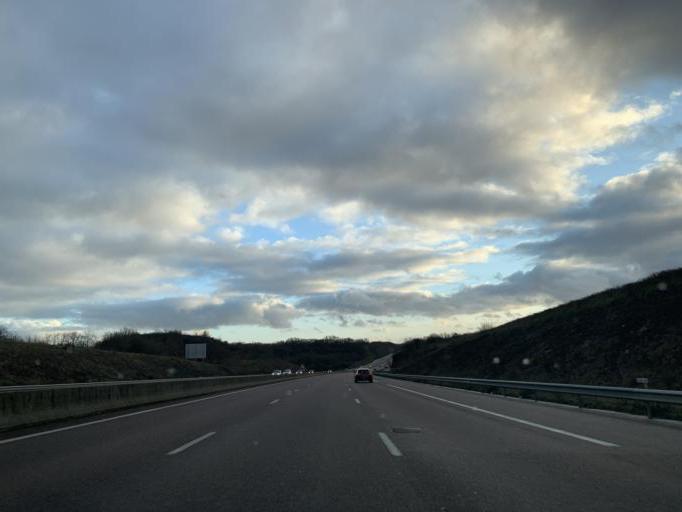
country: FR
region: Bourgogne
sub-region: Departement de la Cote-d'Or
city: Selongey
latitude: 47.7476
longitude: 5.1939
